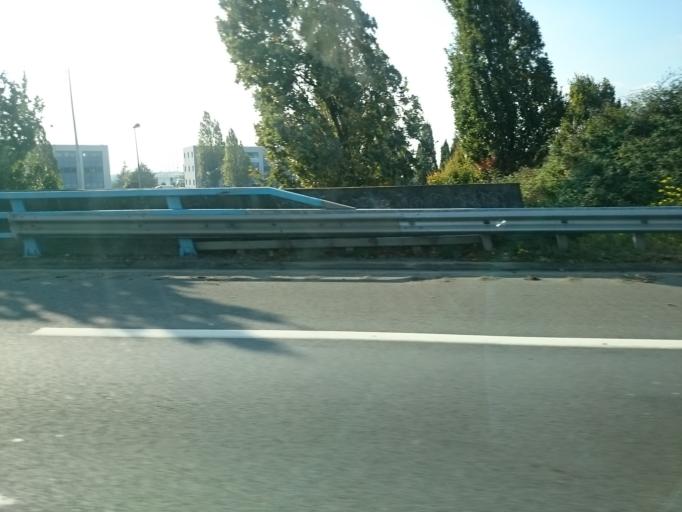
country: FR
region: Pays de la Loire
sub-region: Departement de la Loire-Atlantique
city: Saint-Herblain
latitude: 47.2250
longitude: -1.6217
